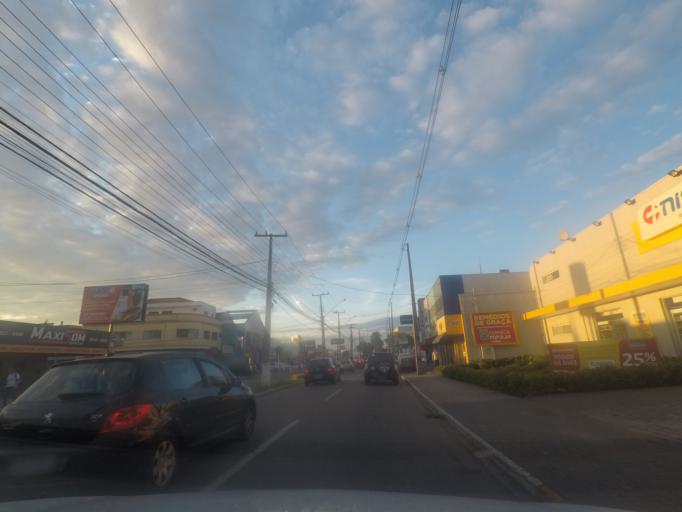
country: BR
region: Parana
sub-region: Pinhais
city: Pinhais
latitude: -25.4304
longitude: -49.1836
